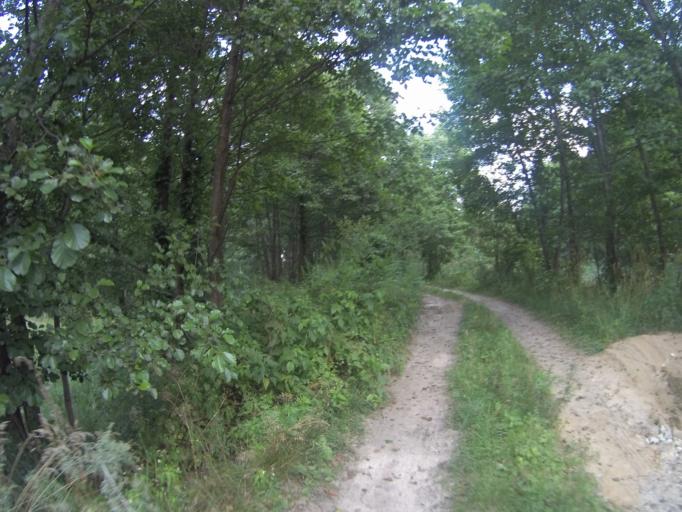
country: RU
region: Vladimir
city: Imeni Vorovskogo
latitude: 55.7378
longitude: 40.9583
